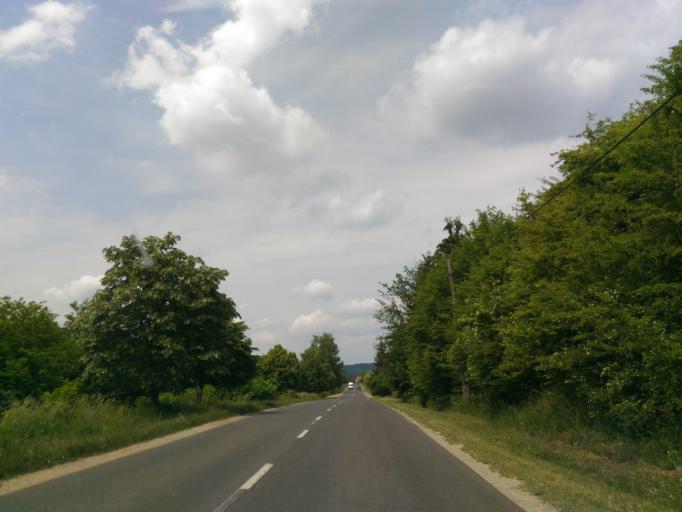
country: HU
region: Baranya
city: Komlo
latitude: 46.2035
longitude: 18.2498
